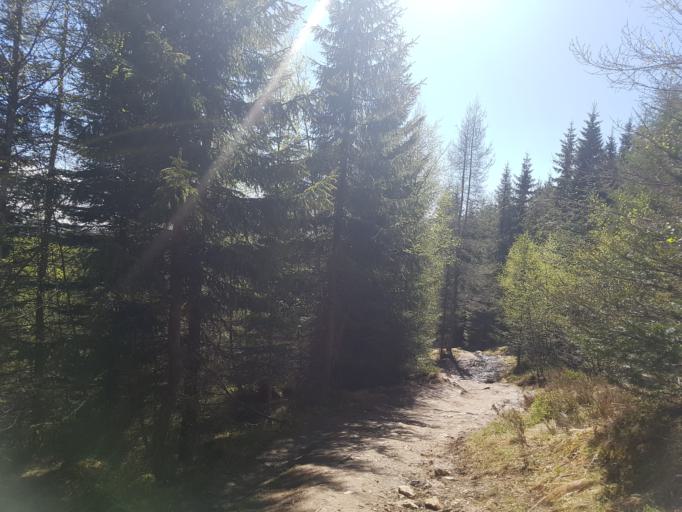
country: NO
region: Sor-Trondelag
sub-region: Trondheim
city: Trondheim
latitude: 63.4255
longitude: 10.3147
